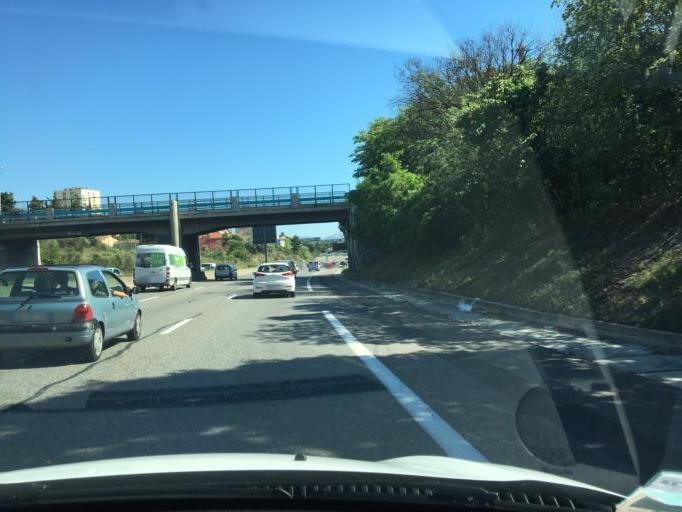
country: FR
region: Provence-Alpes-Cote d'Azur
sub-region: Departement des Bouches-du-Rhone
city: Marseille 15
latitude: 43.3737
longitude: 5.3608
